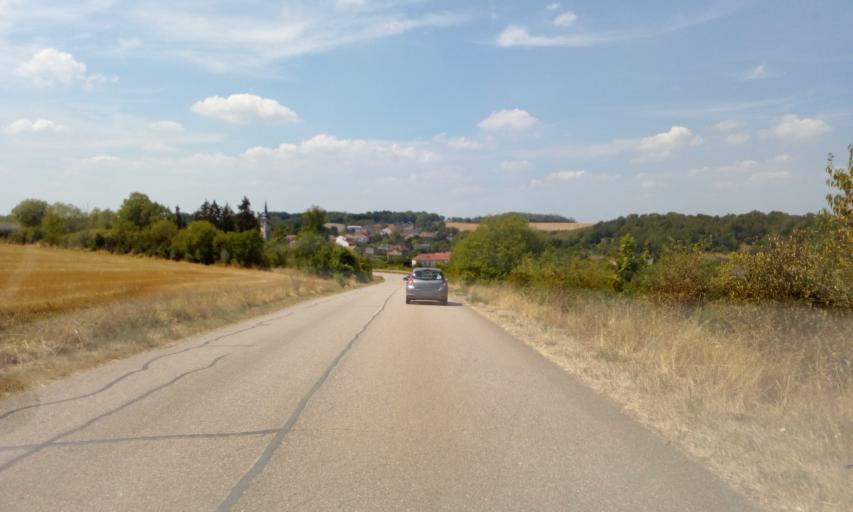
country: FR
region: Lorraine
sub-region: Departement de Meurthe-et-Moselle
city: Pagny-sur-Moselle
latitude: 48.9546
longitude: 5.8739
